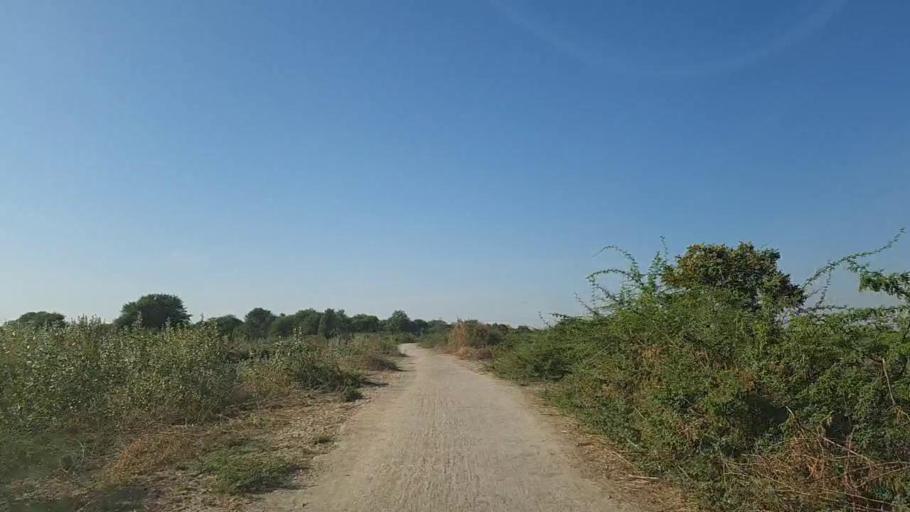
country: PK
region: Sindh
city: Samaro
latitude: 25.2613
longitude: 69.4878
